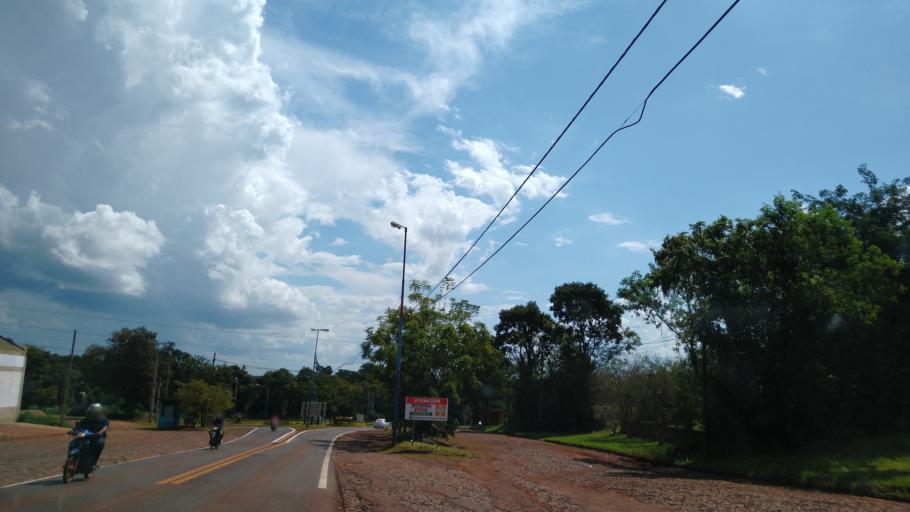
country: AR
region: Misiones
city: Puerto Libertad
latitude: -25.9700
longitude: -54.5776
